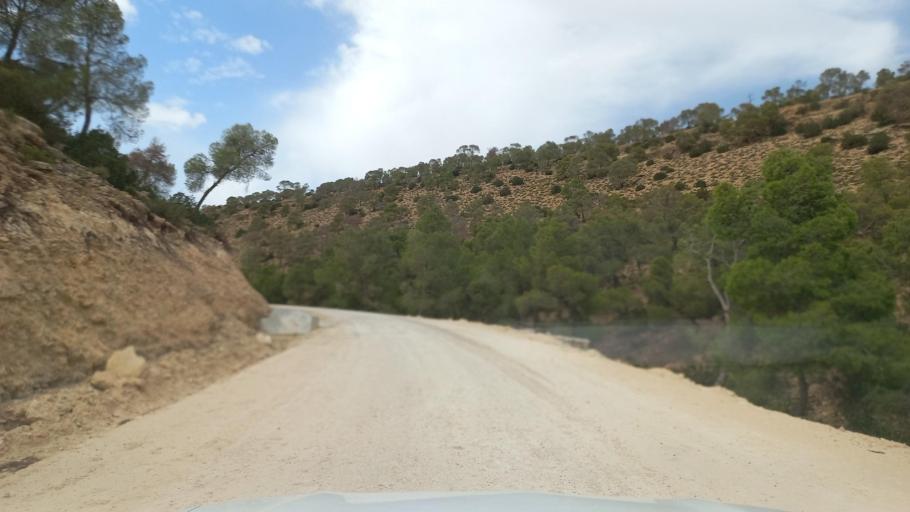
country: TN
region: Al Qasrayn
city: Kasserine
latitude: 35.3767
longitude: 8.8867
